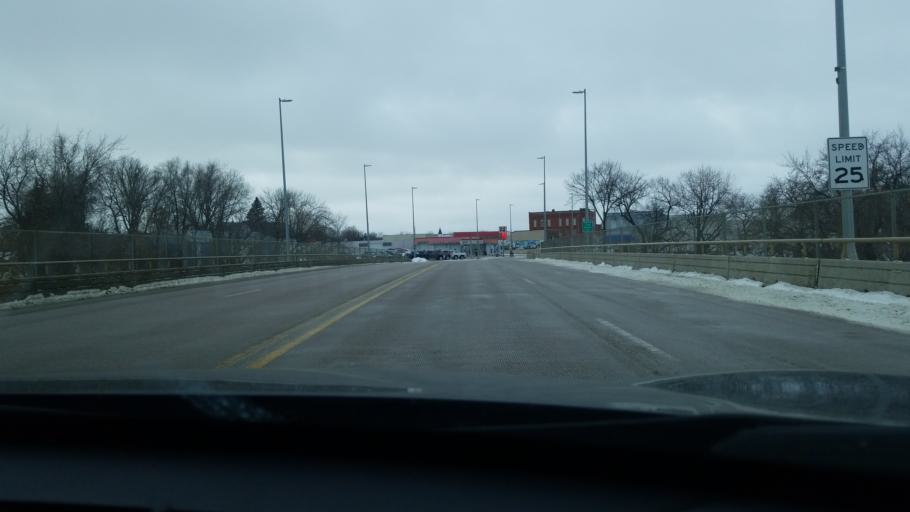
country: US
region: Iowa
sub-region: Lyon County
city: Rock Rapids
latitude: 43.4321
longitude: -96.1638
